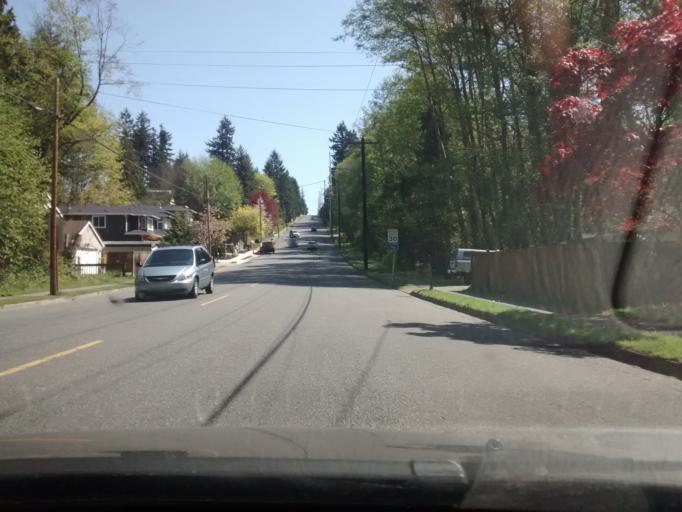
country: US
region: Washington
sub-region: Snohomish County
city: Edmonds
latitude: 47.8104
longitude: -122.3641
